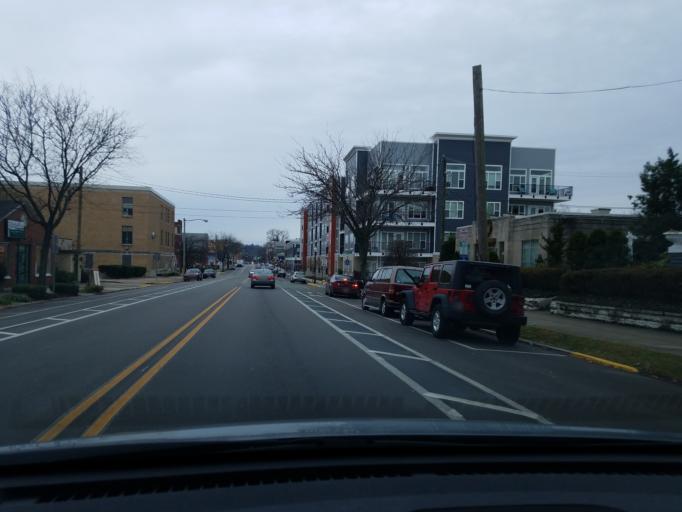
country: US
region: Indiana
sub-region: Floyd County
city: New Albany
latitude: 38.2878
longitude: -85.8173
